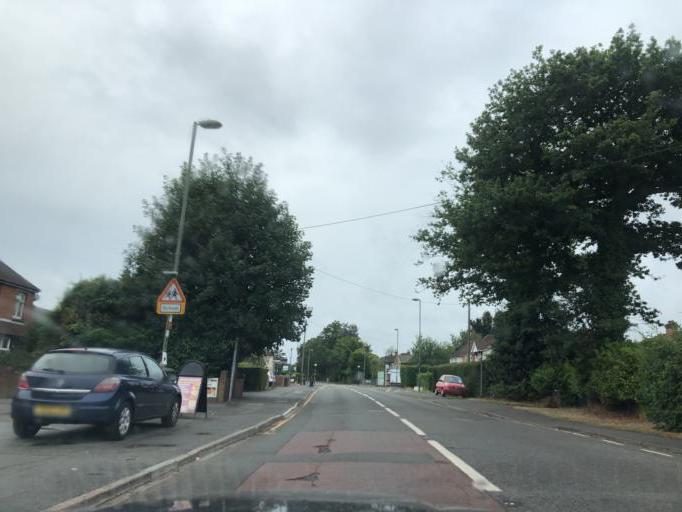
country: GB
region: England
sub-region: Hampshire
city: Farnborough
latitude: 51.2937
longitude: -0.7264
